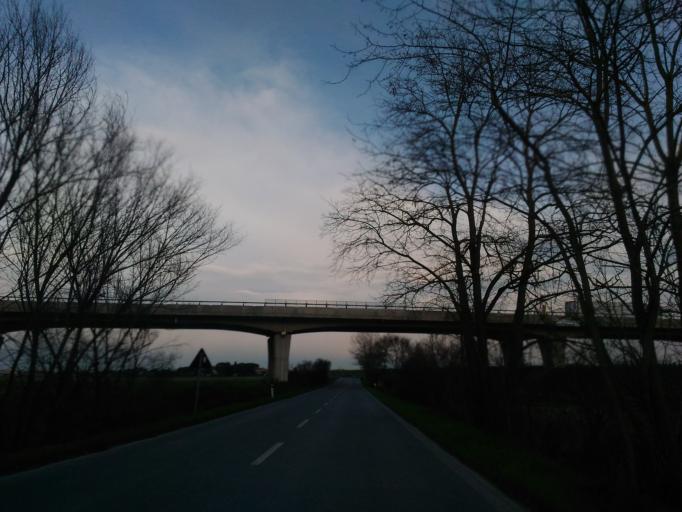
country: IT
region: Tuscany
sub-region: Provincia di Livorno
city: Vicarello
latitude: 43.6019
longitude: 10.4472
